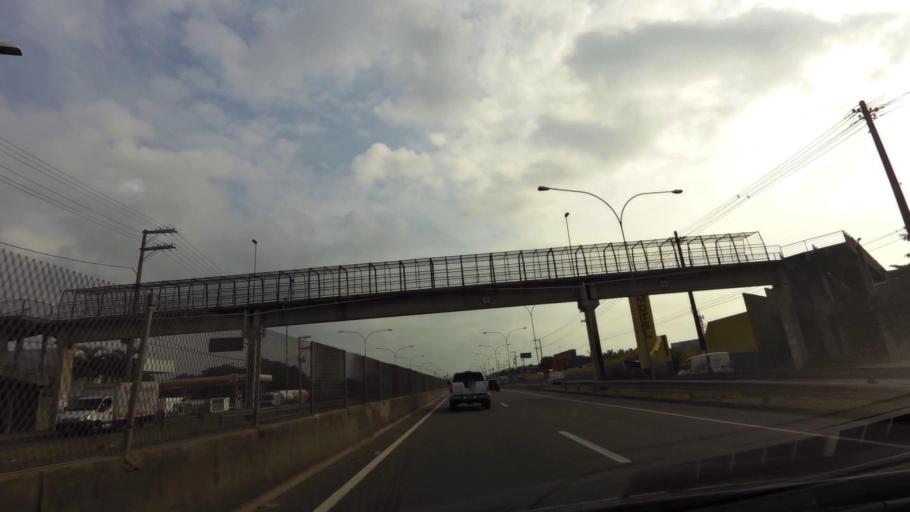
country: BR
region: Espirito Santo
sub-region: Vila Velha
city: Vila Velha
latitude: -20.4246
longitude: -40.3297
